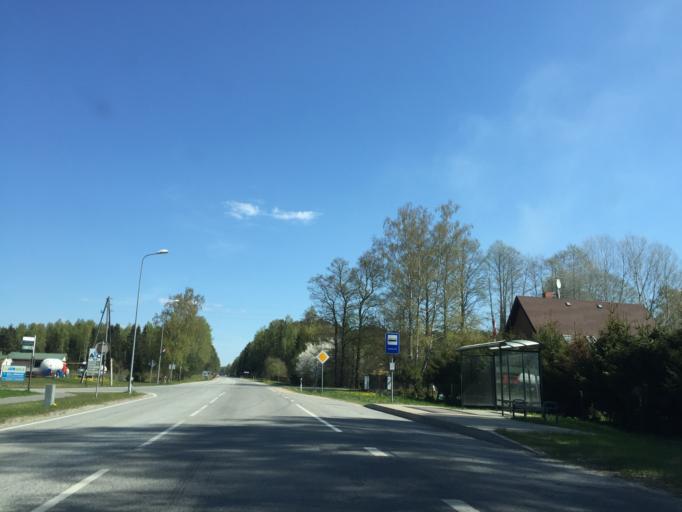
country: LV
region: Saulkrastu
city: Saulkrasti
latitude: 57.3210
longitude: 24.4248
